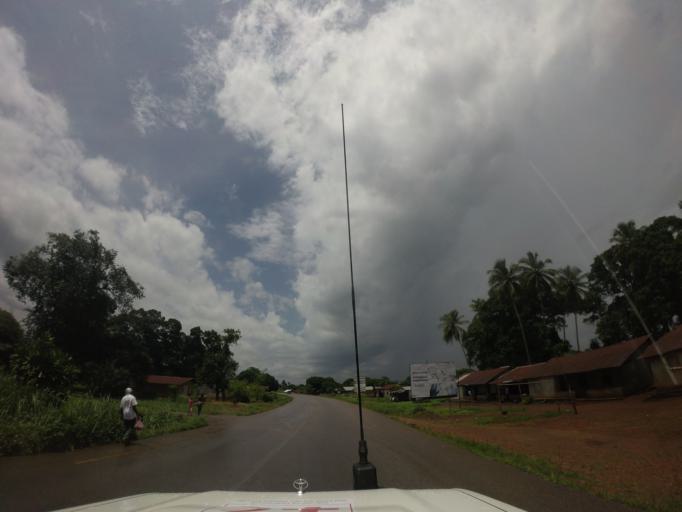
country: SL
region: Southern Province
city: Rotifunk
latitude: 8.4892
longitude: -12.7500
